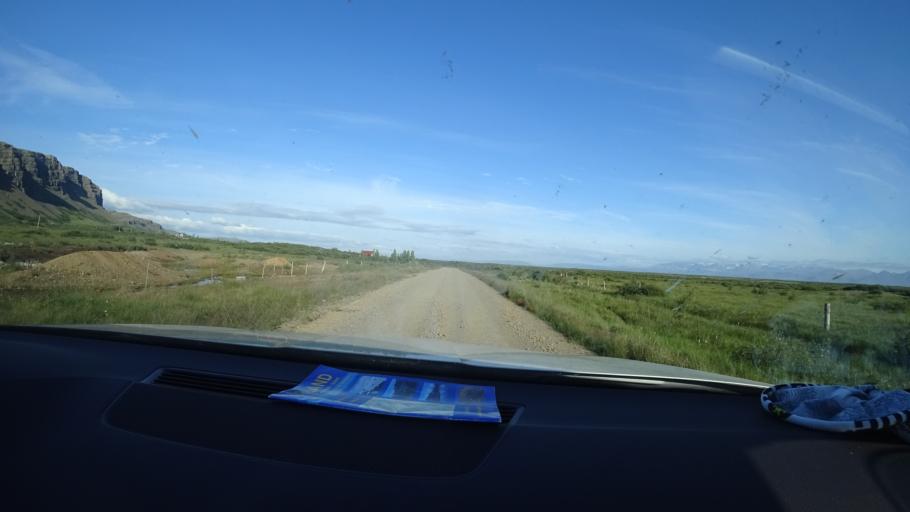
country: IS
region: West
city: Borgarnes
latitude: 64.6915
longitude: -21.9404
